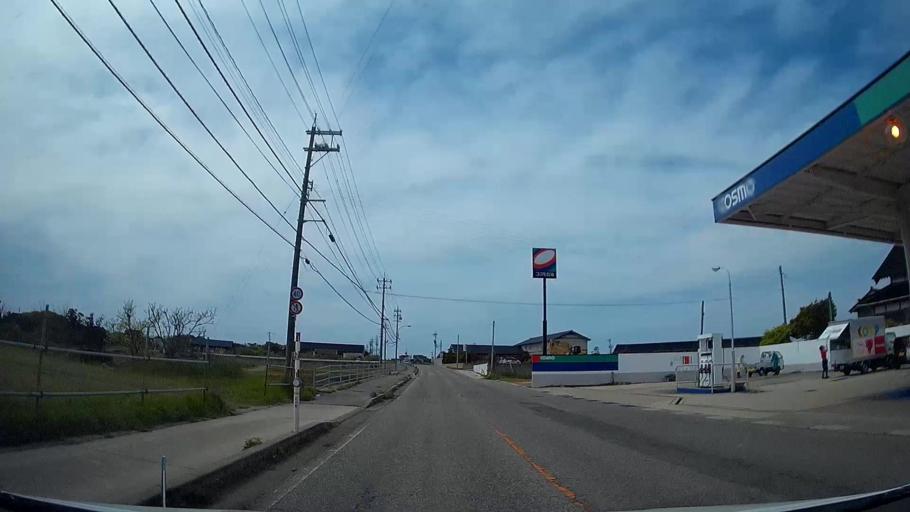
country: JP
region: Ishikawa
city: Hakui
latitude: 37.0097
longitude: 136.7636
